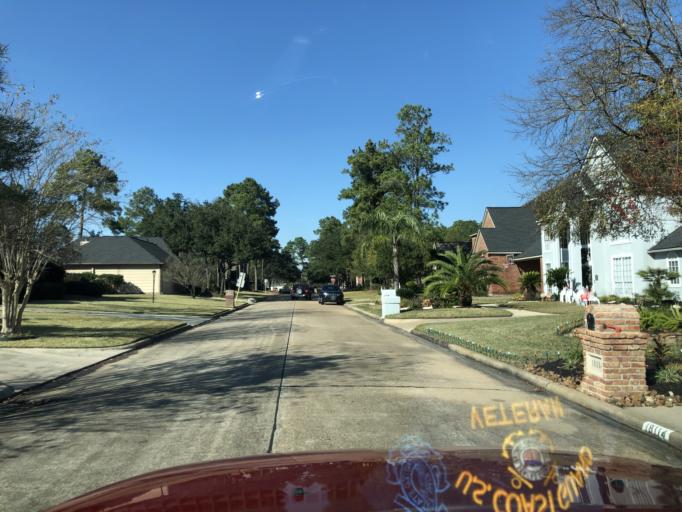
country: US
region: Texas
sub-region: Harris County
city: Tomball
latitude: 30.0320
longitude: -95.5436
